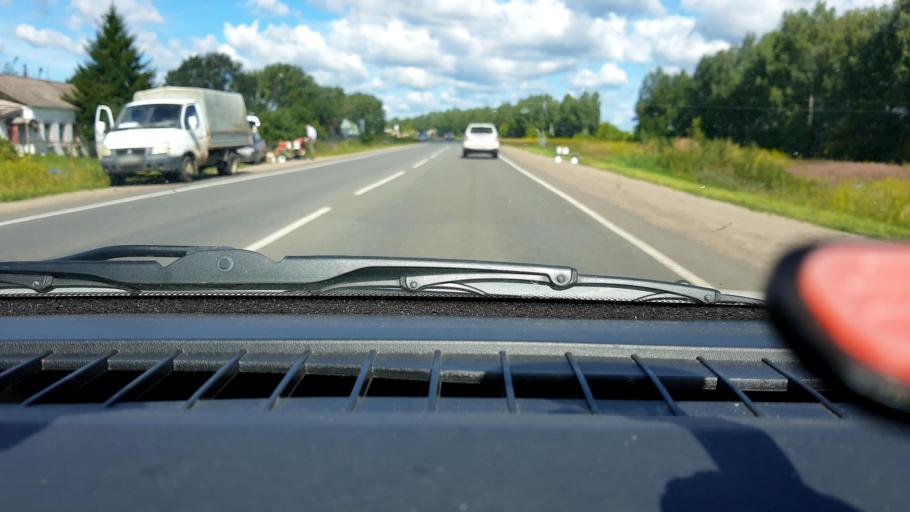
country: RU
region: Nizjnij Novgorod
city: Arzamas
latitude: 55.2946
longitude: 43.9388
